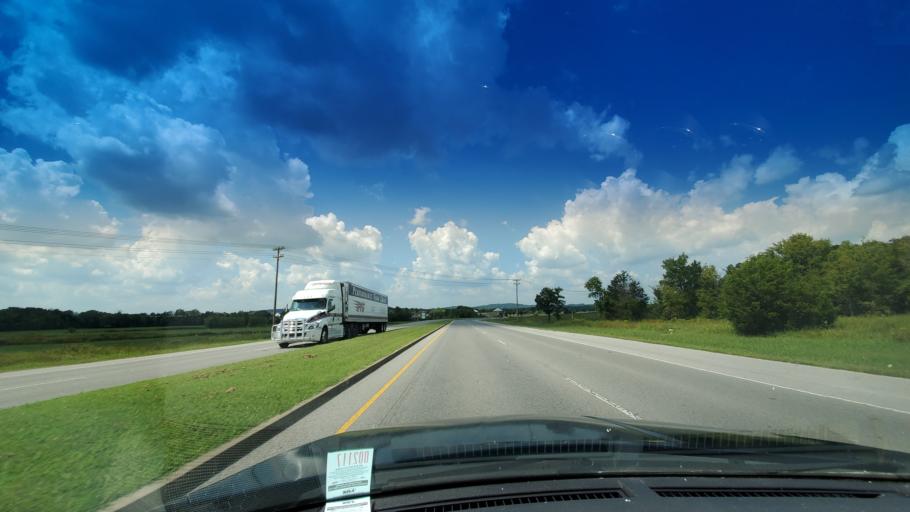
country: US
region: Tennessee
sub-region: Wilson County
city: Lebanon
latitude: 36.1776
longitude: -86.3225
